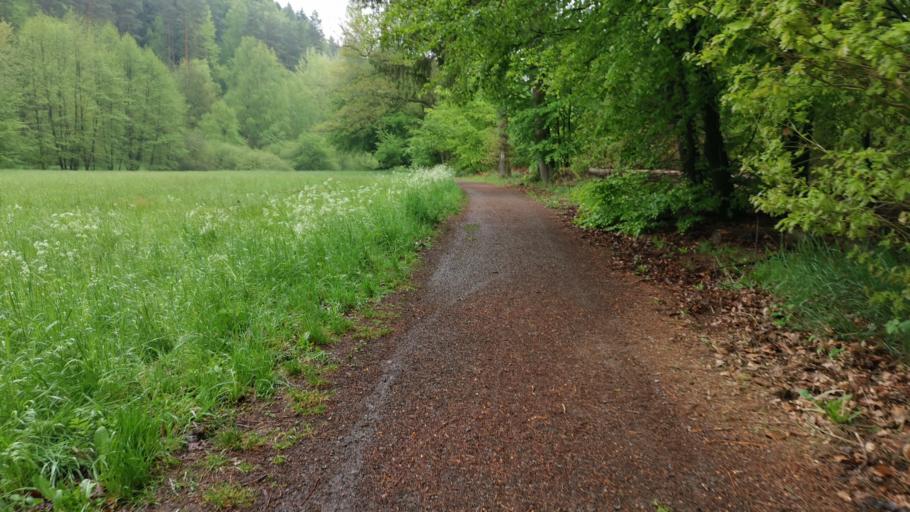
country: DE
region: Saarland
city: Kirkel
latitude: 49.2651
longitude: 7.1868
